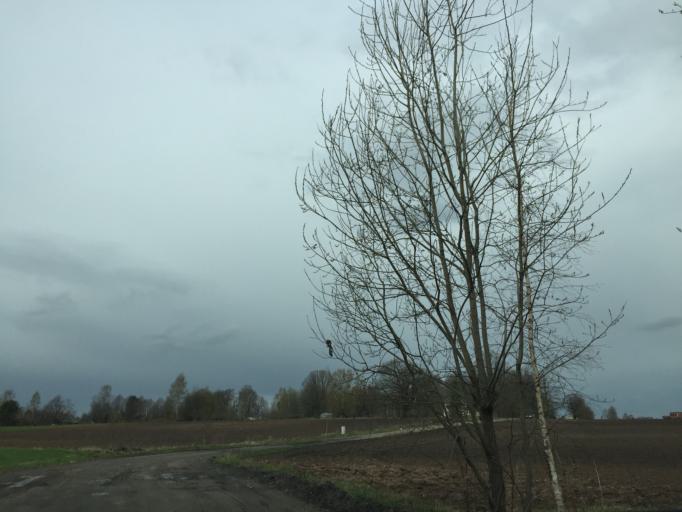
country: LV
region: Priekuli
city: Priekuli
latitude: 57.3060
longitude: 25.3401
